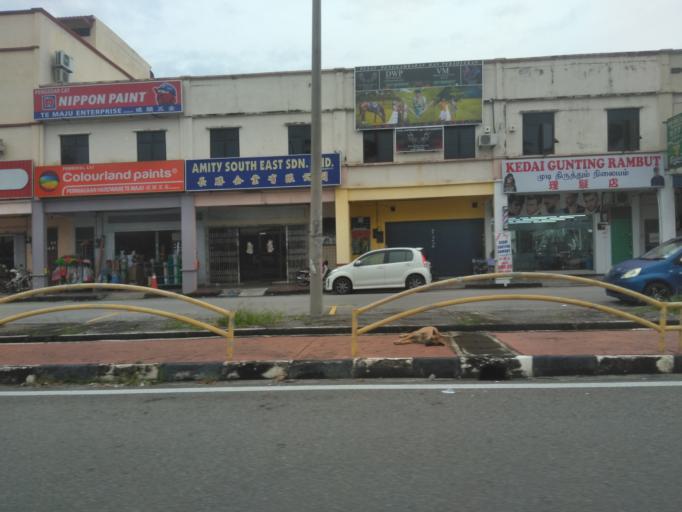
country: MY
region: Penang
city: Bukit Mertajam
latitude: 5.3334
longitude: 100.4810
